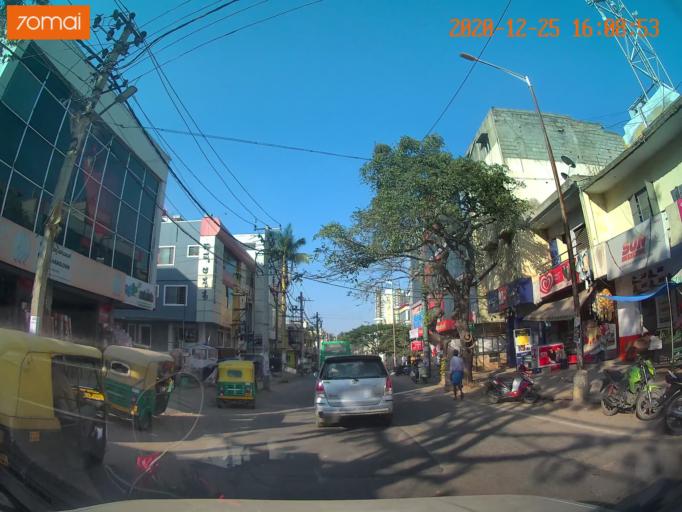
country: IN
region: Karnataka
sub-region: Bangalore Urban
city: Bangalore
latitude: 12.8983
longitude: 77.6265
